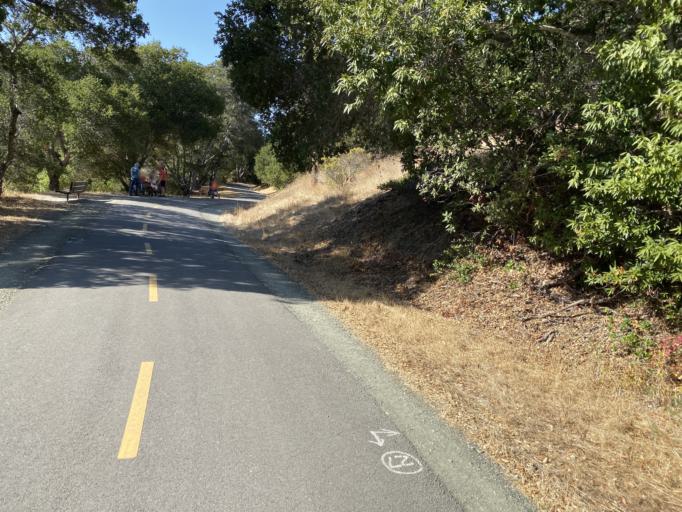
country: US
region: California
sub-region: San Mateo County
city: Hillsborough
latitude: 37.5492
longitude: -122.3840
